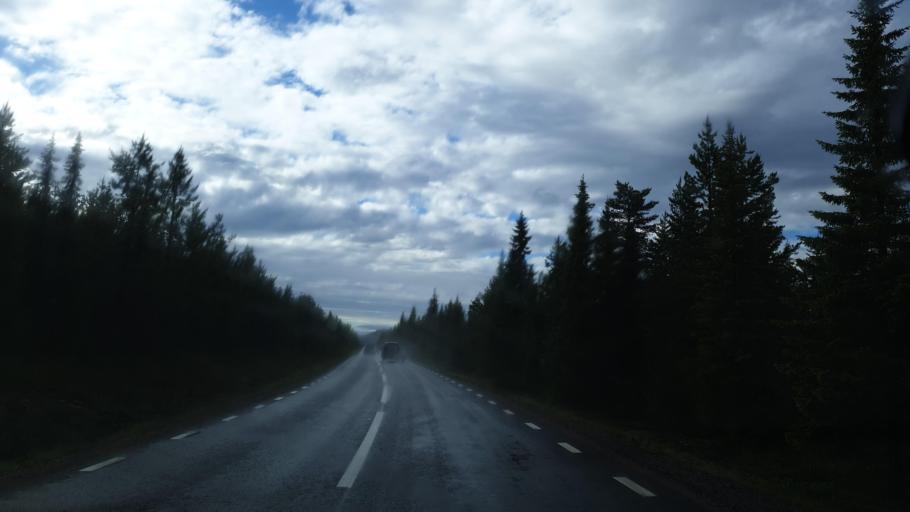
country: SE
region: Norrbotten
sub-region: Arjeplogs Kommun
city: Arjeplog
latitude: 65.8378
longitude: 18.4258
